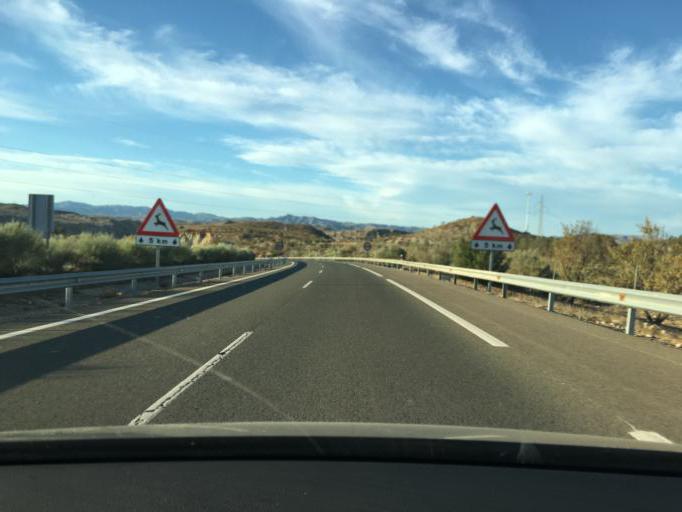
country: ES
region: Andalusia
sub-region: Provincia de Almeria
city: Sorbas
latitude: 37.0805
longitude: -2.0562
